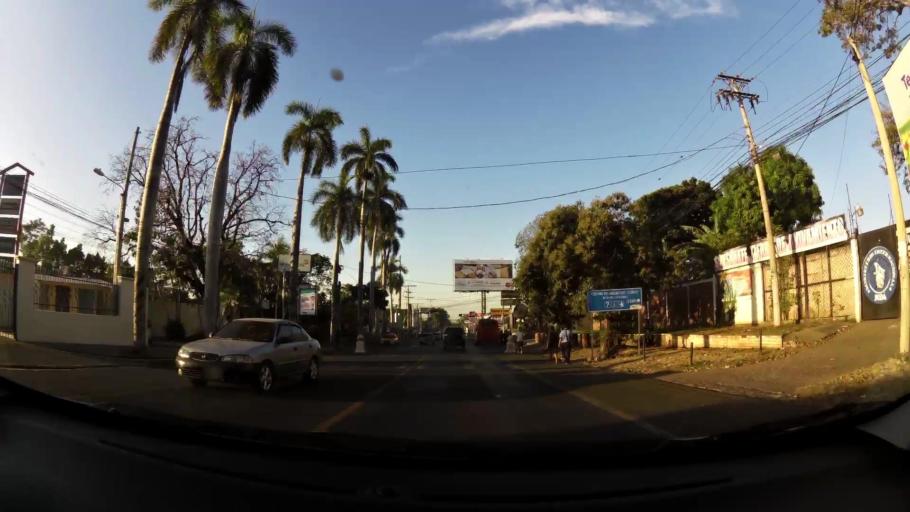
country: SV
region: Sonsonate
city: Sonsonate
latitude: 13.7211
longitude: -89.7201
